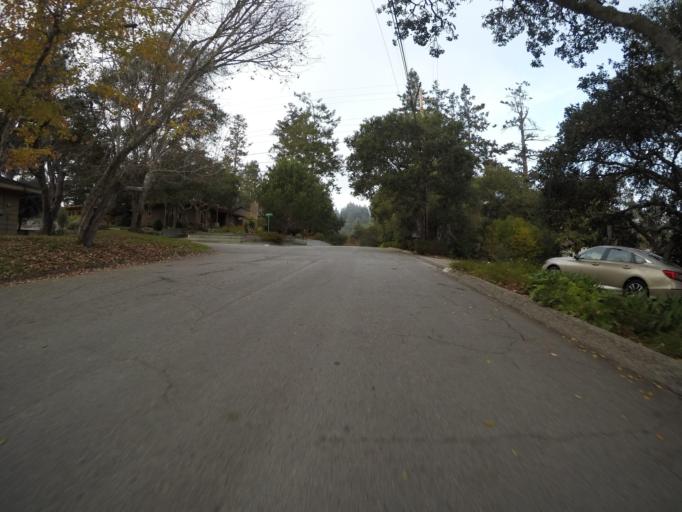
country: US
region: California
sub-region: Santa Cruz County
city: Pasatiempo
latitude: 37.0189
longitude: -122.0335
